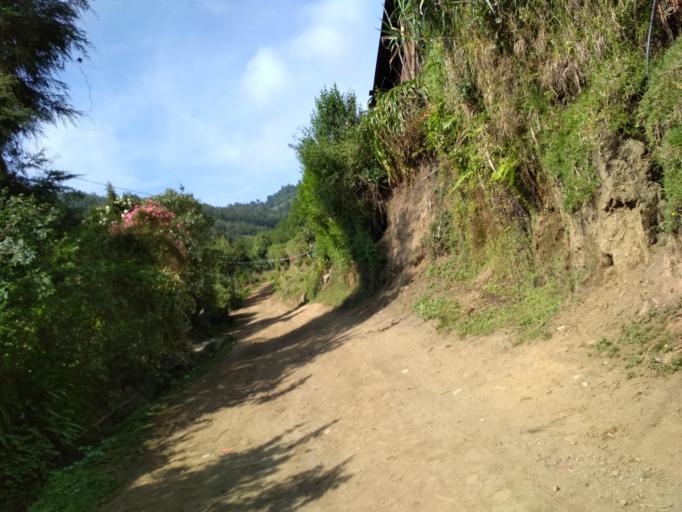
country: MX
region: Veracruz
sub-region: Mariano Escobedo
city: San Isidro el Berro
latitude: 18.9435
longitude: -97.2175
